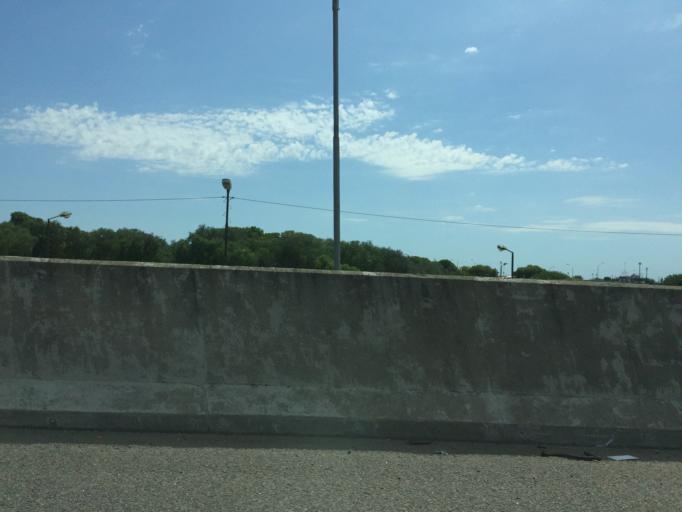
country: AR
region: Buenos Aires F.D.
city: Retiro
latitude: -34.5710
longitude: -58.4016
